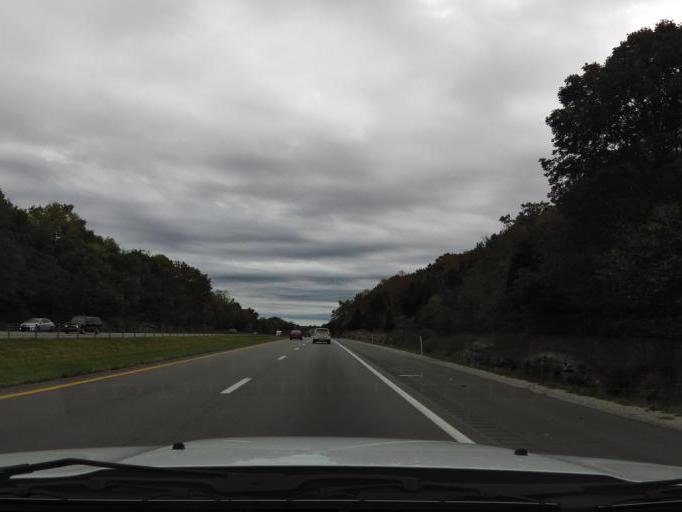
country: US
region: Kentucky
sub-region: Rockcastle County
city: Mount Vernon
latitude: 37.4028
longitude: -84.3386
